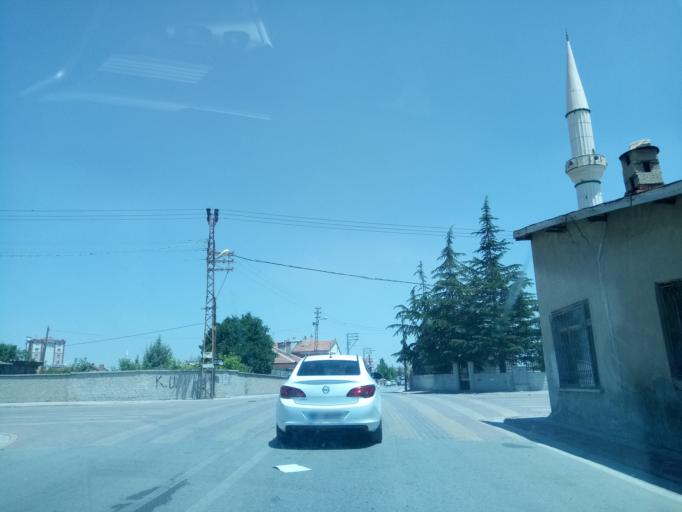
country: TR
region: Konya
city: Meram
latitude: 37.8382
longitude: 32.4932
